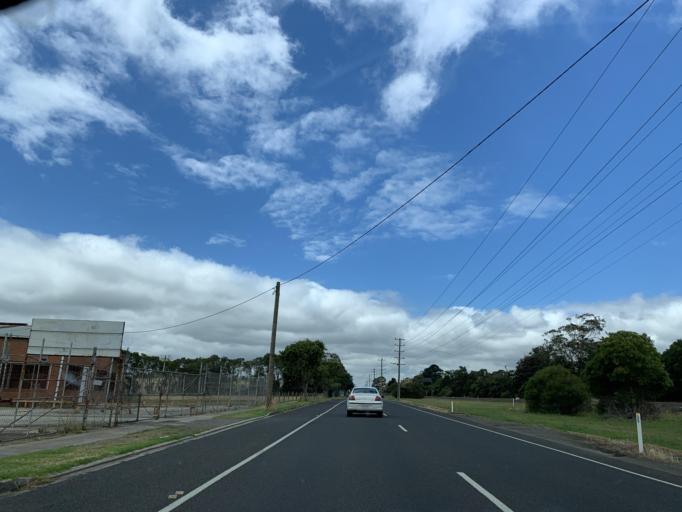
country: AU
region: Victoria
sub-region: Latrobe
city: Moe
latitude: -38.1814
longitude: 146.2441
